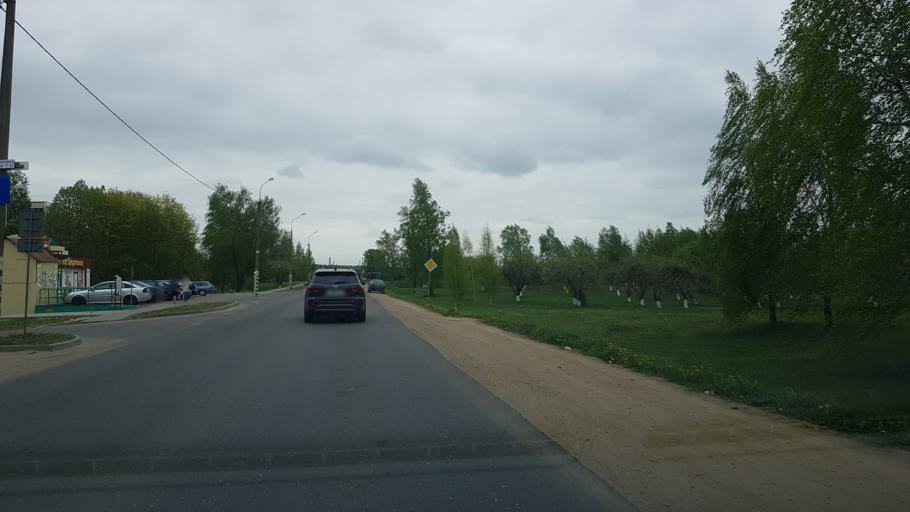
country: BY
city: Fanipol
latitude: 53.7390
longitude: 27.3174
